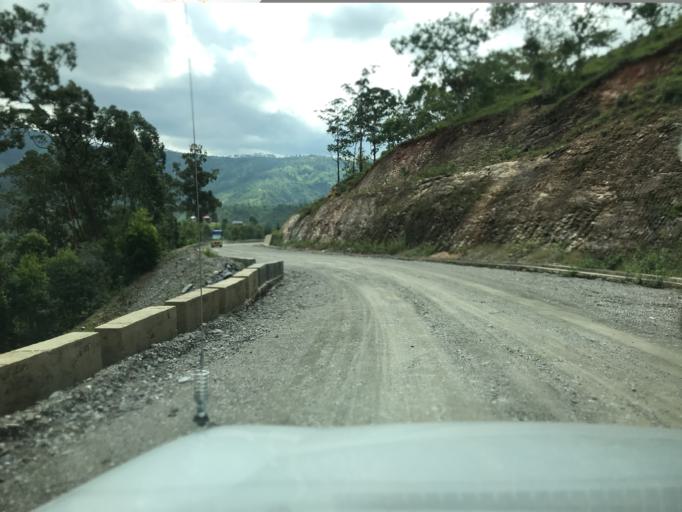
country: TL
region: Aileu
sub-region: Aileu Villa
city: Aileu
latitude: -8.6641
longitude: 125.5407
